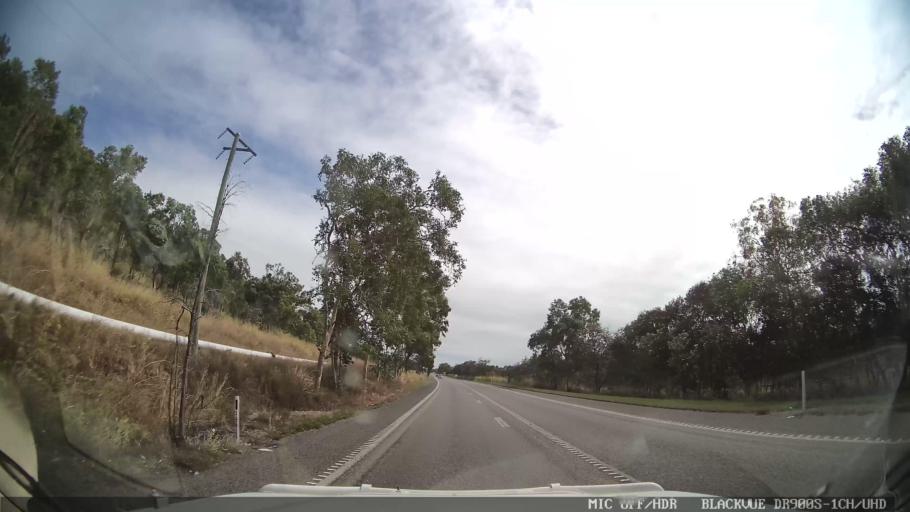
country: AU
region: Queensland
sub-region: Hinchinbrook
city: Ingham
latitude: -19.0081
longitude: 146.3619
